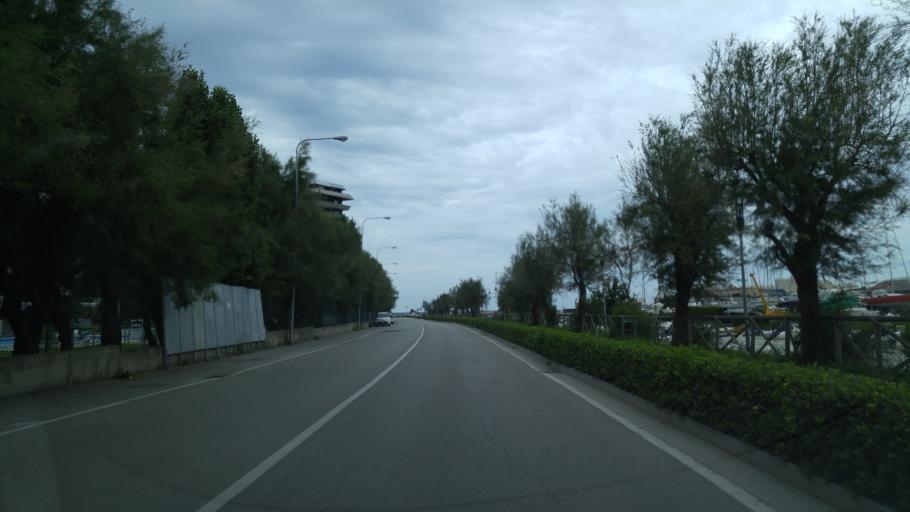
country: IT
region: The Marches
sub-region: Provincia di Pesaro e Urbino
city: Pesaro
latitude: 43.9199
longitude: 12.9025
